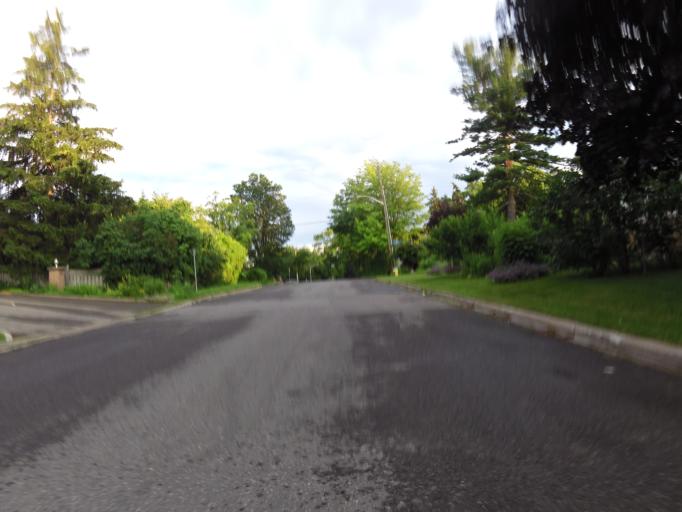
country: CA
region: Ontario
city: Bells Corners
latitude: 45.3623
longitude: -75.7865
